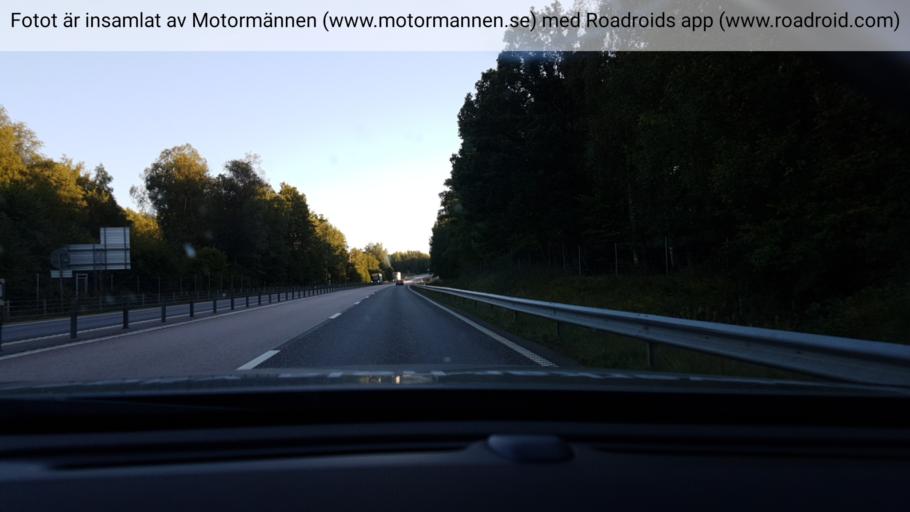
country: SE
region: Halland
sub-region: Halmstads Kommun
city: Oskarstrom
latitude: 56.8210
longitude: 12.9627
